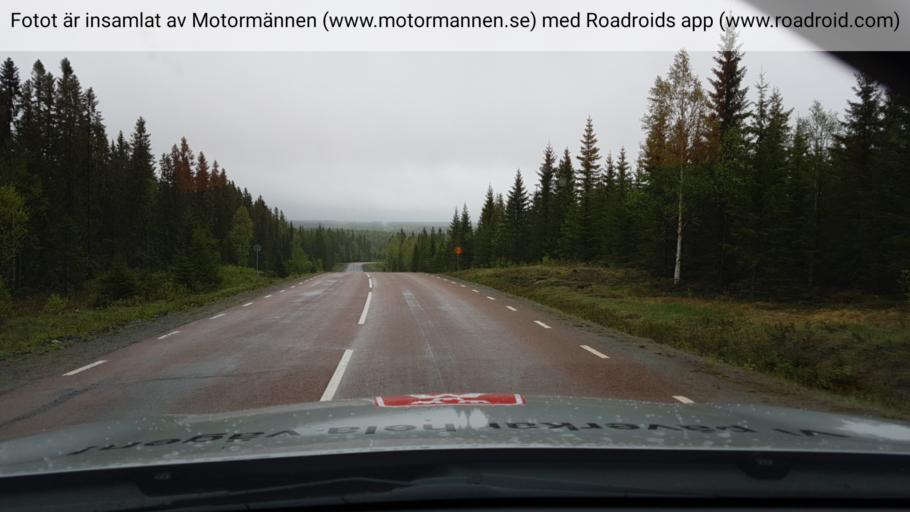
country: SE
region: Jaemtland
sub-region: Krokoms Kommun
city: Valla
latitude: 63.1497
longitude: 13.9551
